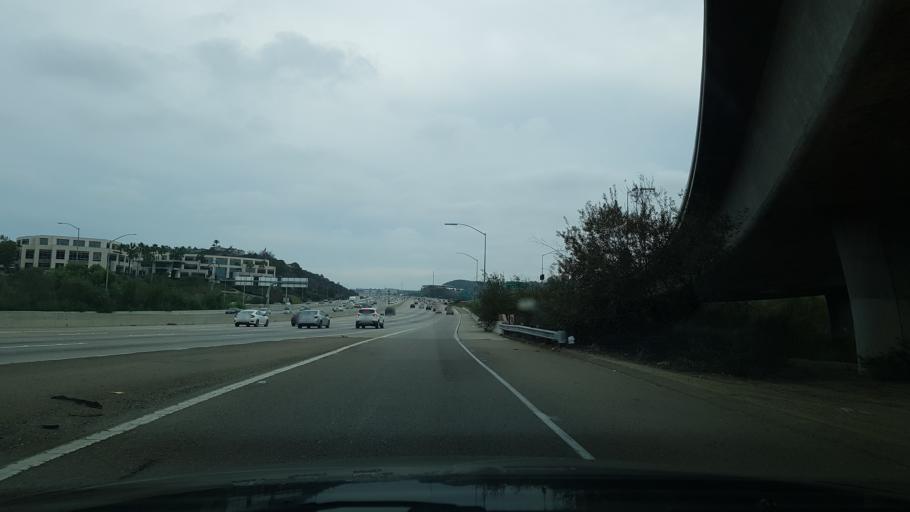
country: US
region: California
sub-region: San Diego County
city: Del Mar
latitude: 32.9308
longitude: -117.2413
